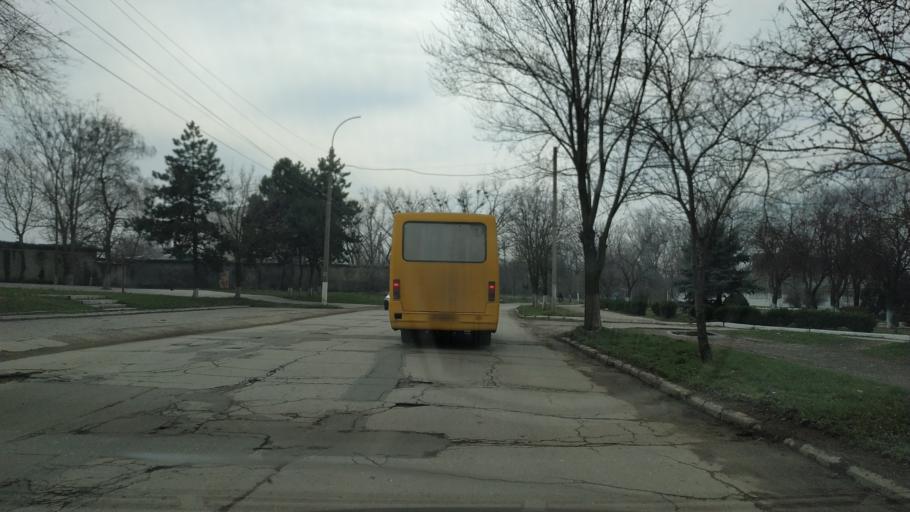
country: MD
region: Cahul
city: Cahul
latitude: 45.8921
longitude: 28.2004
